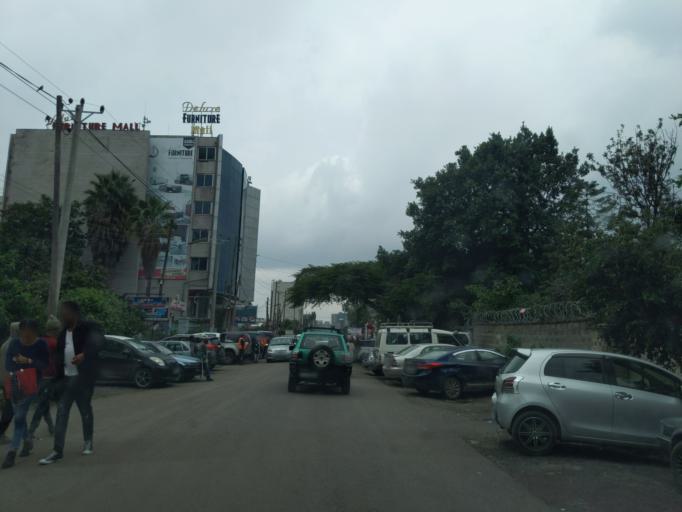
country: ET
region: Adis Abeba
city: Addis Ababa
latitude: 8.9995
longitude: 38.7677
